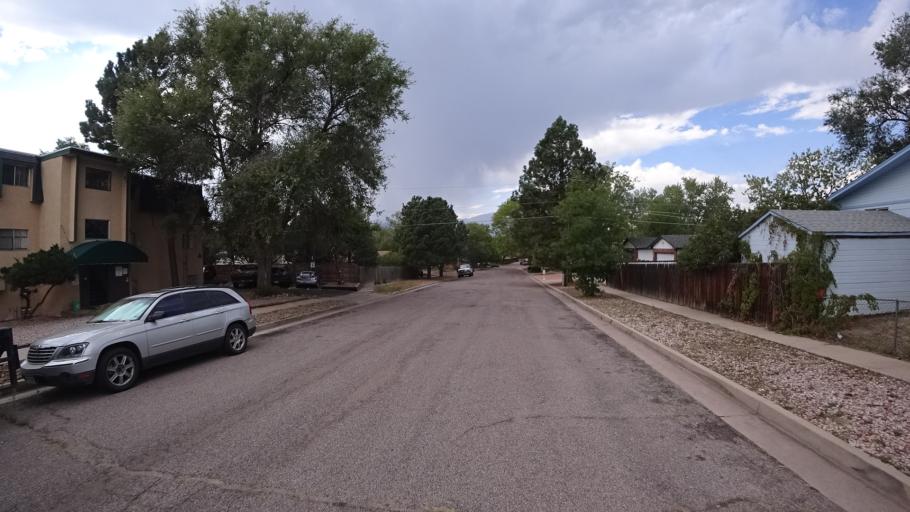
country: US
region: Colorado
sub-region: El Paso County
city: Colorado Springs
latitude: 38.8498
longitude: -104.7617
